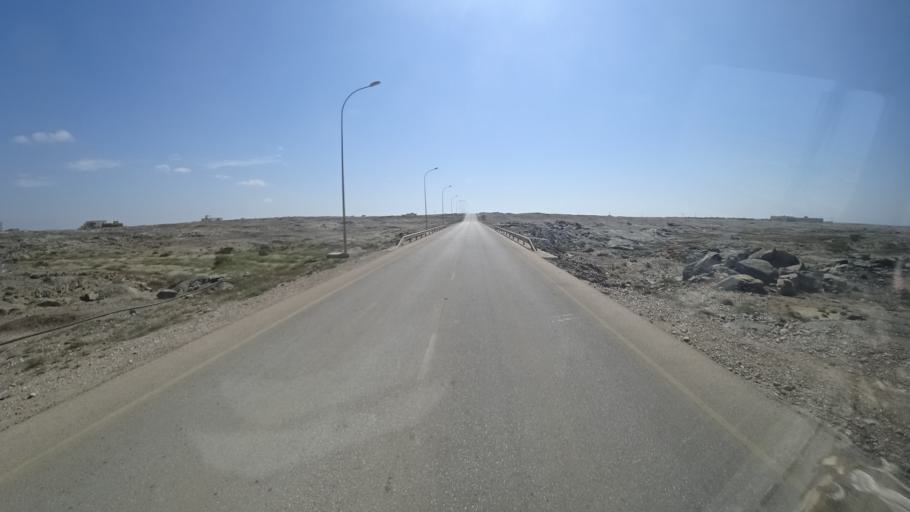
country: OM
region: Zufar
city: Salalah
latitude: 16.9687
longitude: 54.7300
